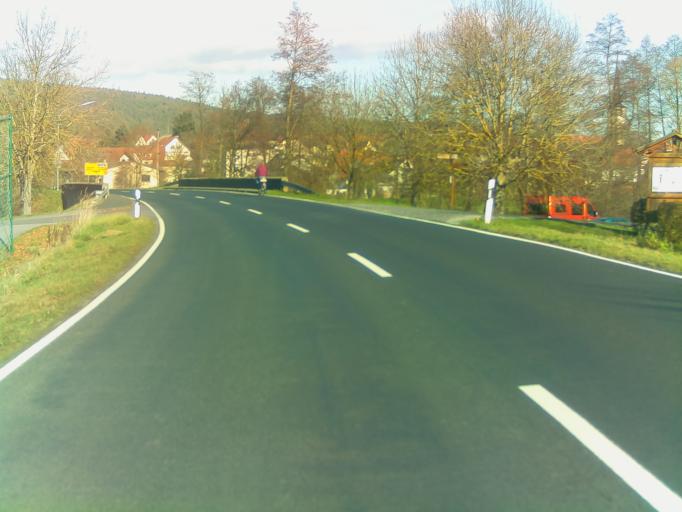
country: DE
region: Bavaria
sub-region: Regierungsbezirk Unterfranken
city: Bad Bocklet
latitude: 50.2825
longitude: 10.0955
